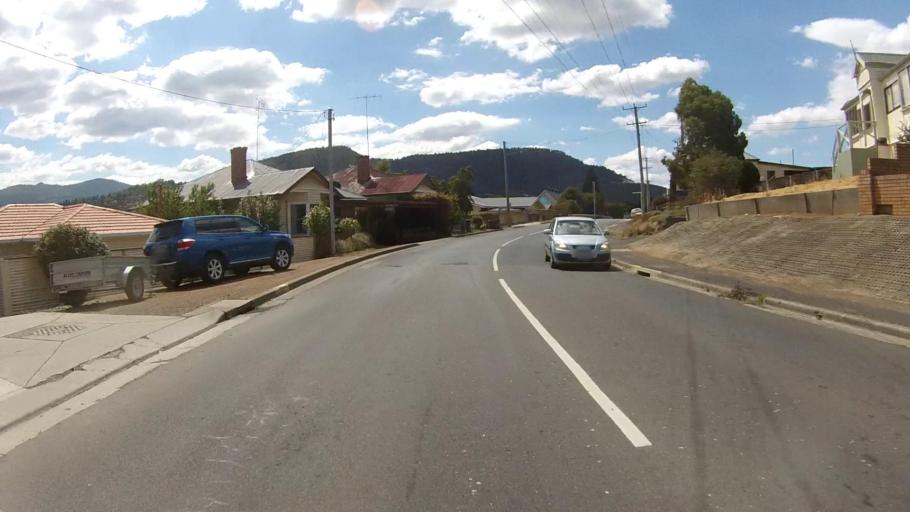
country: AU
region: Tasmania
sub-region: Derwent Valley
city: New Norfolk
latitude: -42.7818
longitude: 147.0536
